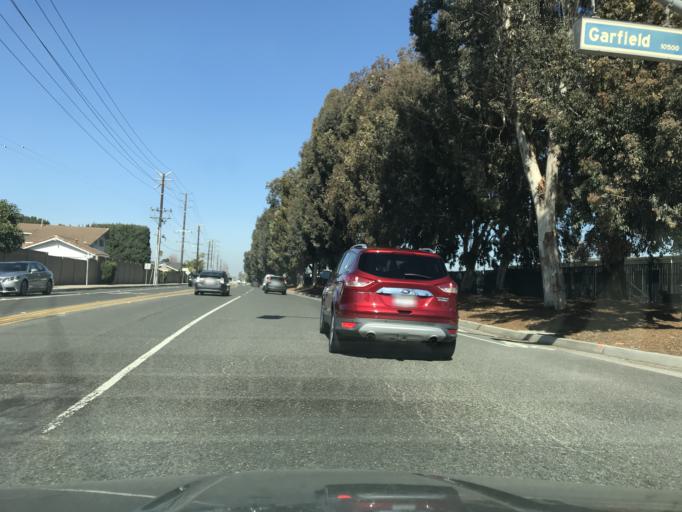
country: US
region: California
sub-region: Orange County
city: Fountain Valley
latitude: 33.6870
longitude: -117.9454
